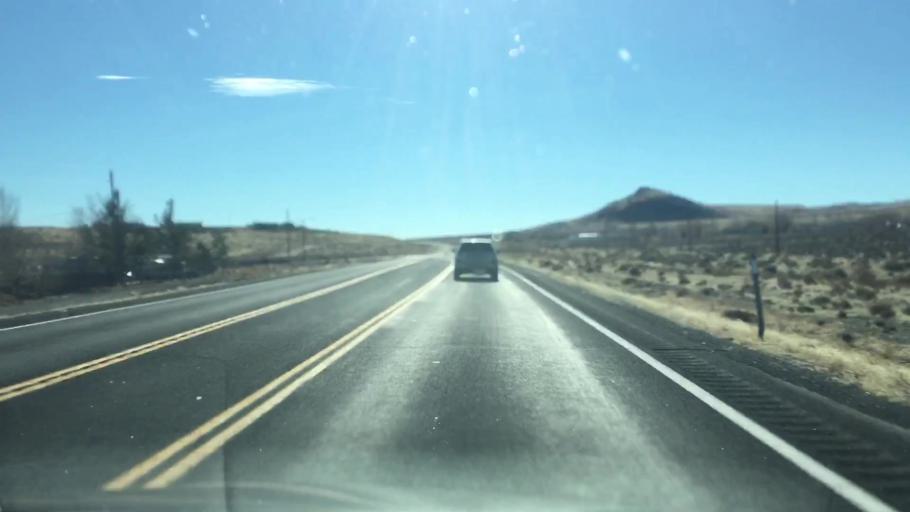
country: US
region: Nevada
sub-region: Lyon County
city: Silver Springs
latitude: 39.3481
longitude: -119.2394
